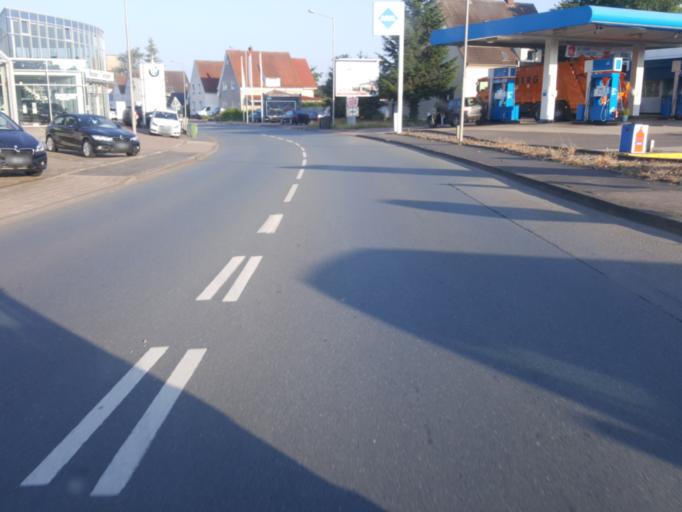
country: DE
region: North Rhine-Westphalia
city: Buende
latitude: 52.2037
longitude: 8.5893
